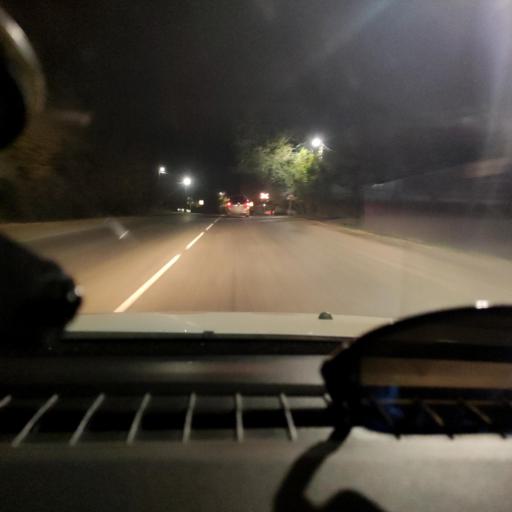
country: RU
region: Samara
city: Rozhdestveno
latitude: 53.1252
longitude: 50.0561
